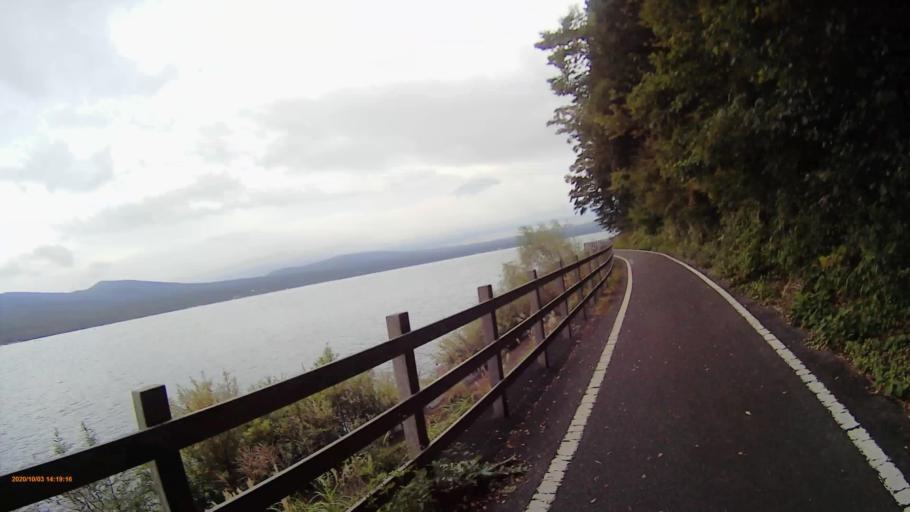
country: JP
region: Shizuoka
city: Gotemba
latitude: 35.4213
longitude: 138.8882
